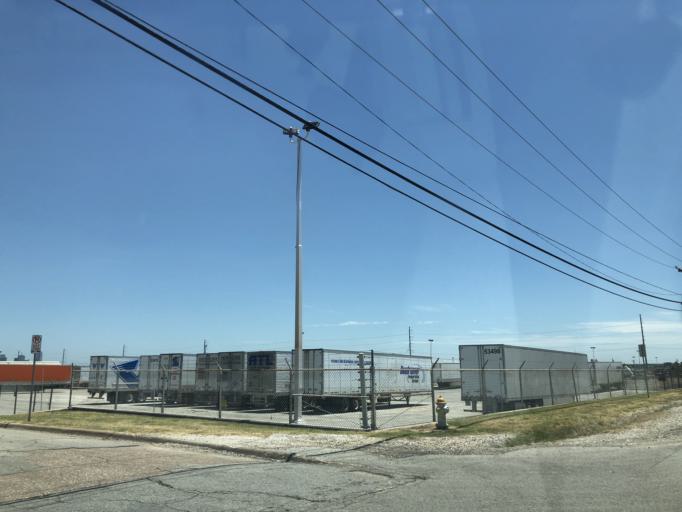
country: US
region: Texas
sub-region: Dallas County
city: Irving
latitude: 32.8127
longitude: -96.8897
